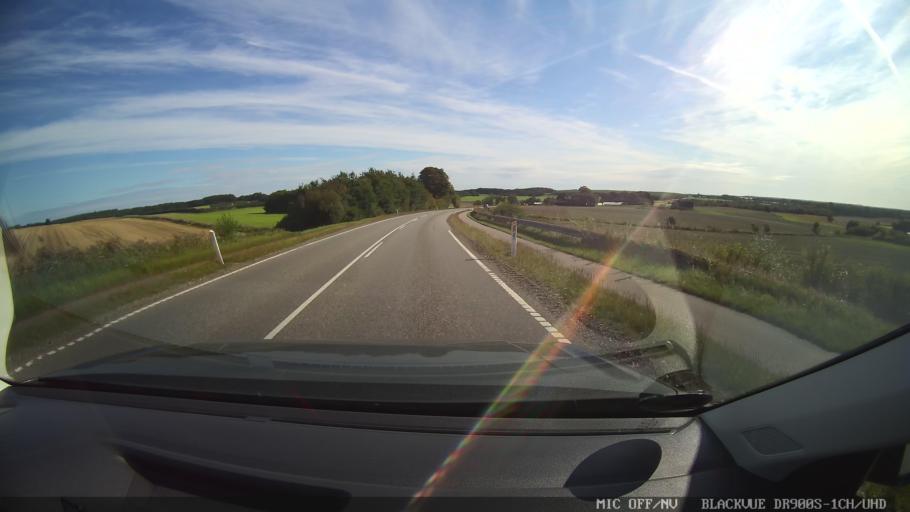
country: DK
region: North Denmark
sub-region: Mariagerfjord Kommune
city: Arden
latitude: 56.7733
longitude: 9.8255
